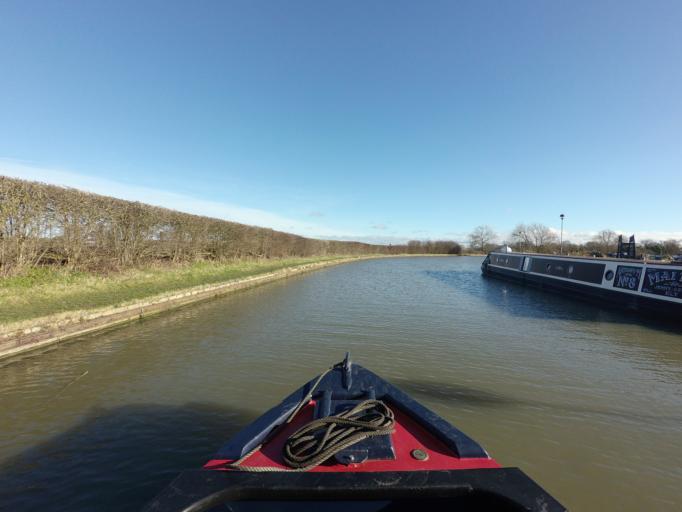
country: GB
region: England
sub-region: Northamptonshire
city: Bugbrooke
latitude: 52.2129
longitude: -1.0250
